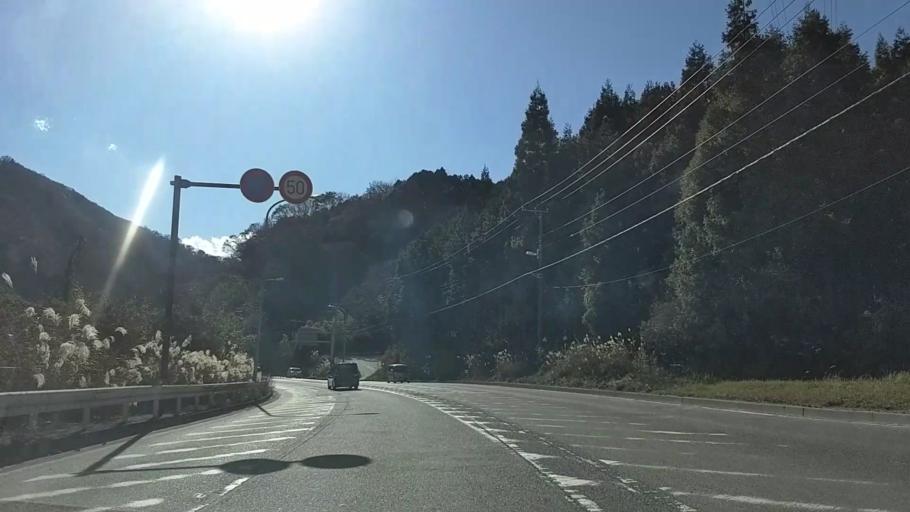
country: JP
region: Shizuoka
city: Gotemba
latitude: 35.3663
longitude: 139.0183
